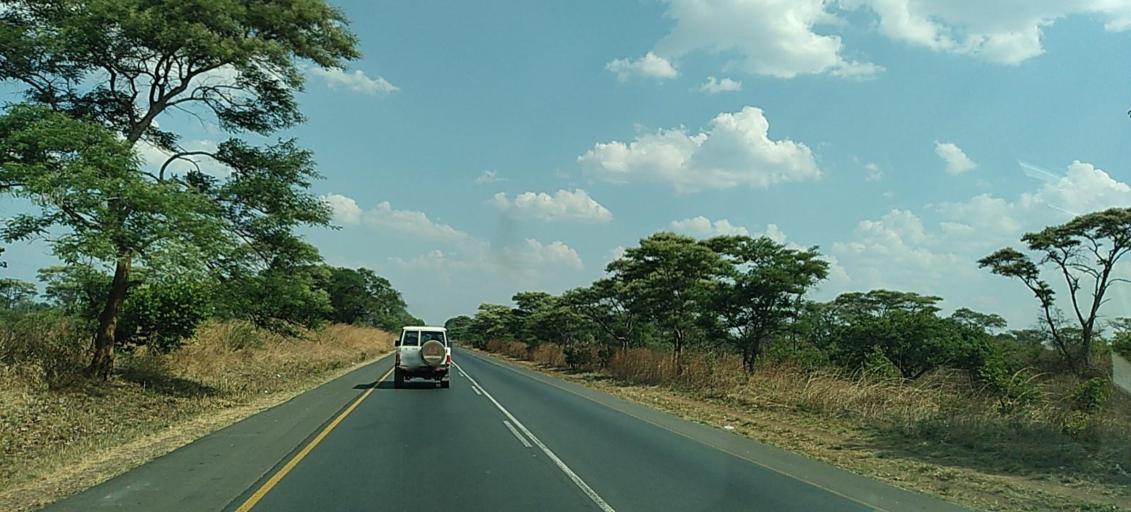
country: ZM
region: Central
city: Chibombo
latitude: -14.8702
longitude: 28.0562
